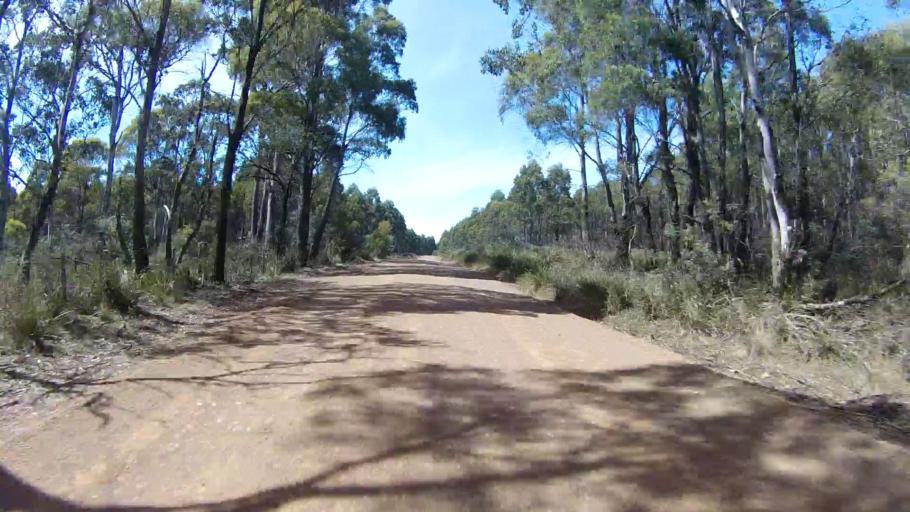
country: AU
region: Tasmania
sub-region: Sorell
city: Sorell
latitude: -42.6870
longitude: 147.7327
